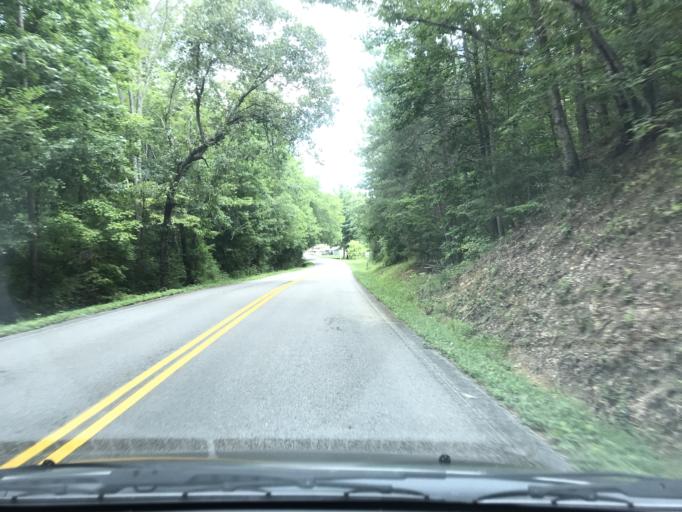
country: US
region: Tennessee
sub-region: Hamilton County
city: Lakesite
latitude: 35.1717
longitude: -85.0861
